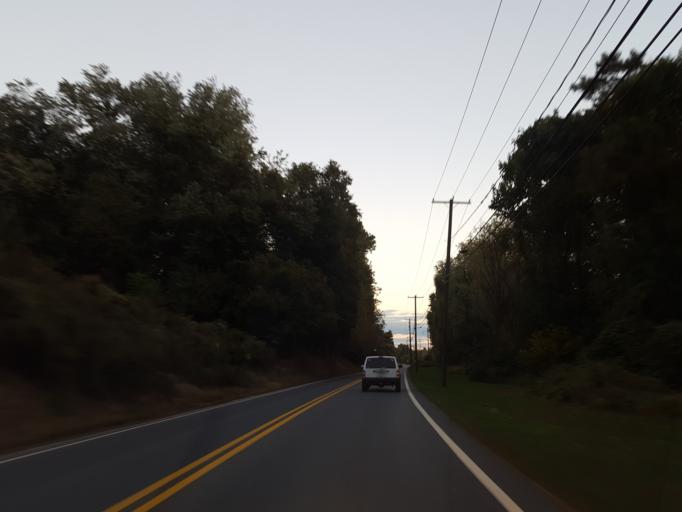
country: US
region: Pennsylvania
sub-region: Lancaster County
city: Columbia
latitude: 40.0084
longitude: -76.4802
